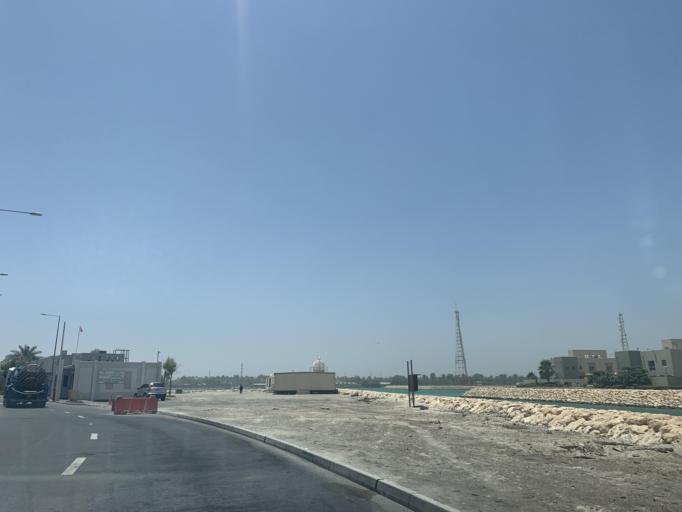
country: BH
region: Manama
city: Jidd Hafs
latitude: 26.2382
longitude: 50.4719
